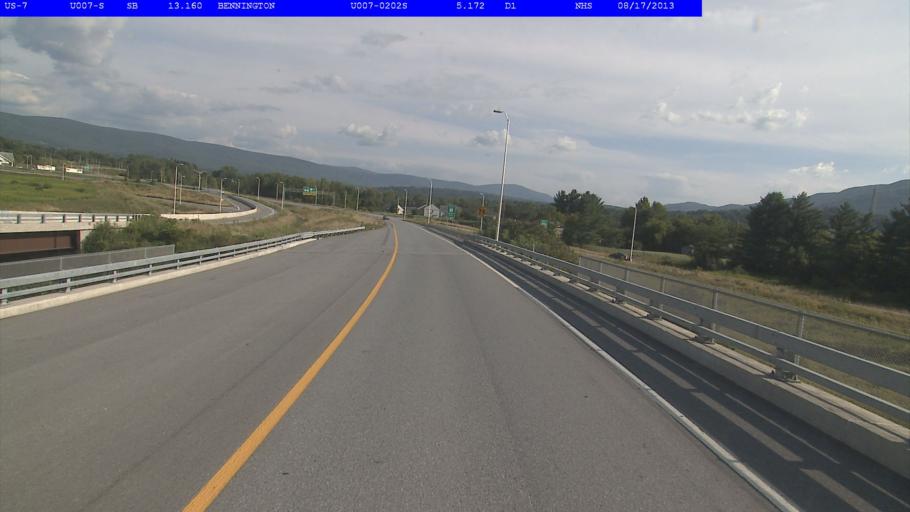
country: US
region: Vermont
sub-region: Bennington County
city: Bennington
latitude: 42.9058
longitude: -73.2083
